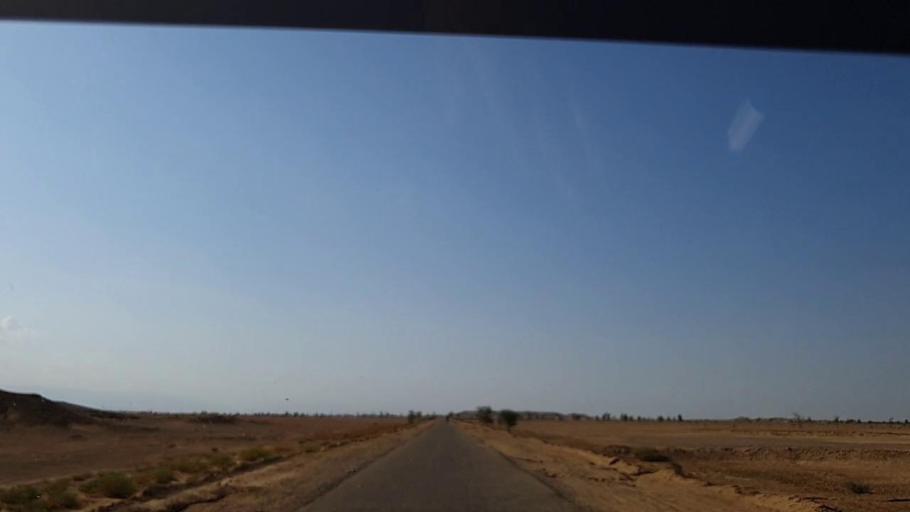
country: PK
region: Sindh
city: Johi
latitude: 26.5260
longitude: 67.5103
